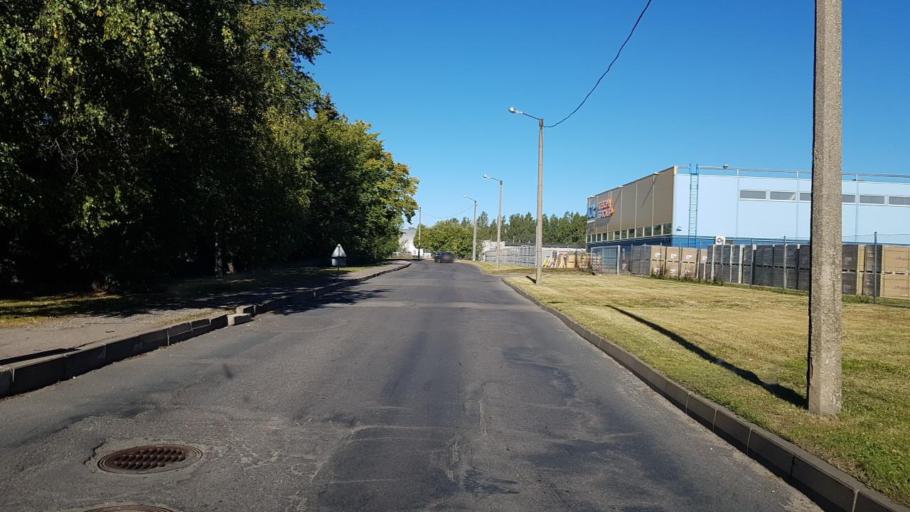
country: EE
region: Harju
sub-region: Tallinna linn
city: Tallinn
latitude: 59.4074
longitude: 24.8154
